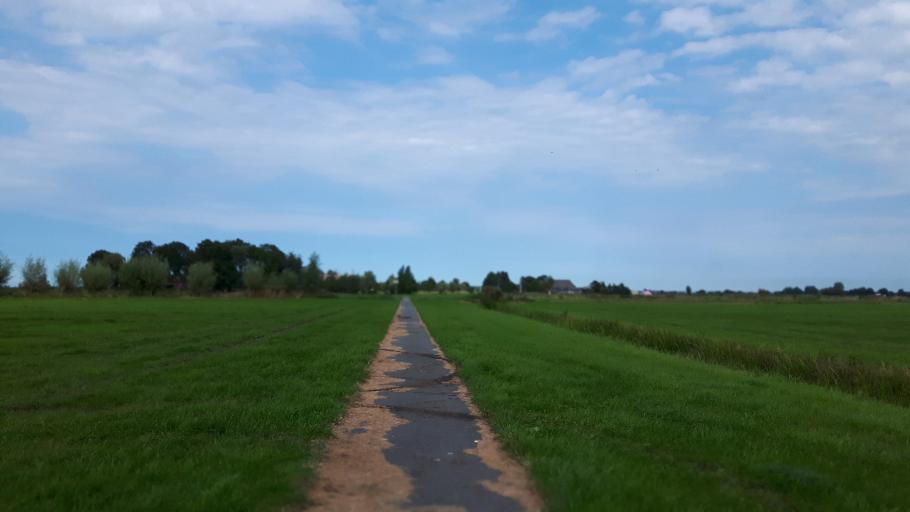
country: NL
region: Friesland
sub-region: Gemeente Leeuwarden
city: Camminghaburen
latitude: 53.2321
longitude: 5.8247
